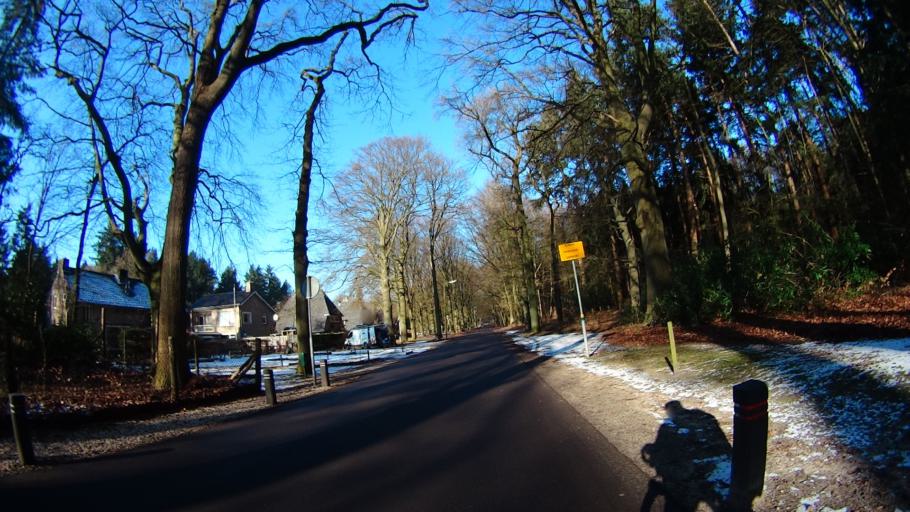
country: NL
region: North Holland
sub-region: Gemeente Hilversum
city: Hilversum
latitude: 52.1823
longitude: 5.2216
